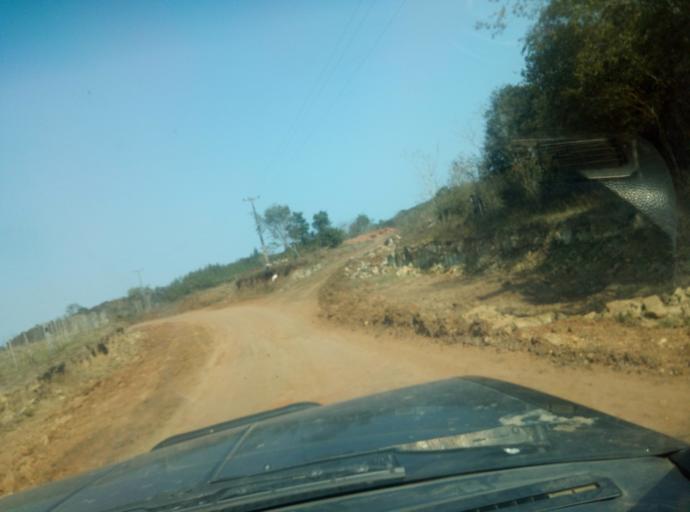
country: PY
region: Caaguazu
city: Coronel Oviedo
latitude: -25.3325
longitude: -56.3140
